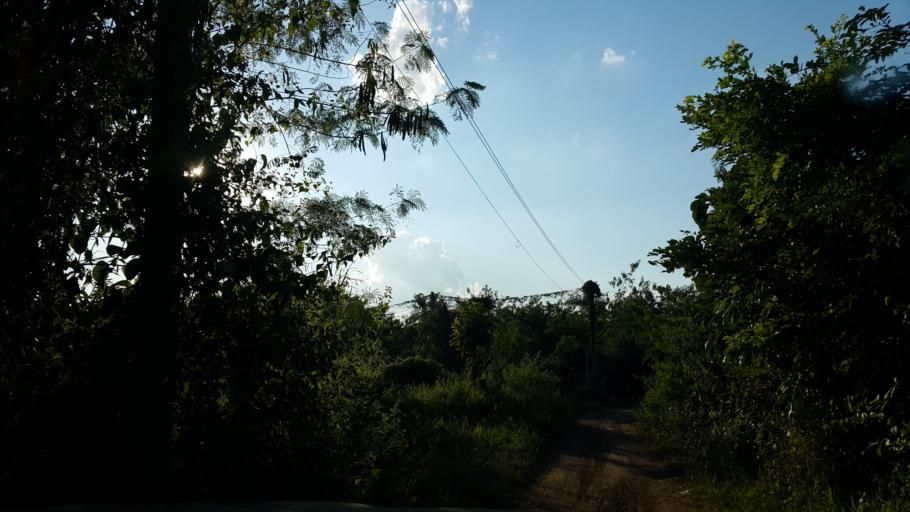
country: TH
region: Chiang Mai
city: Mae On
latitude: 18.7531
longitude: 99.2609
